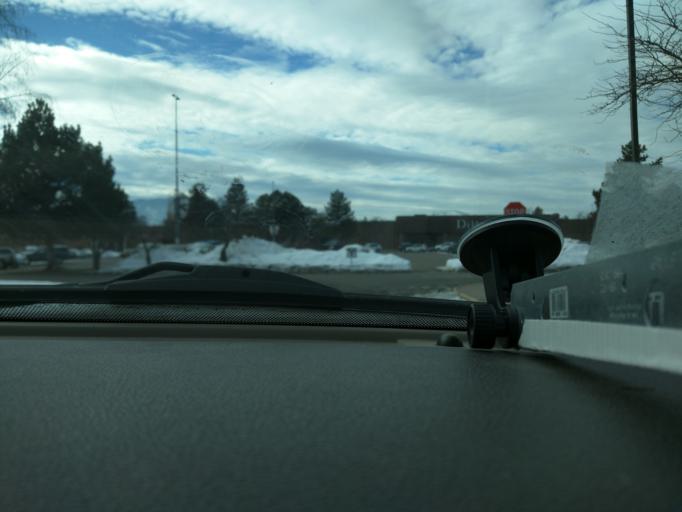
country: US
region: Montana
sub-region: Missoula County
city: Orchard Homes
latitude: 46.8470
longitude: -114.0247
